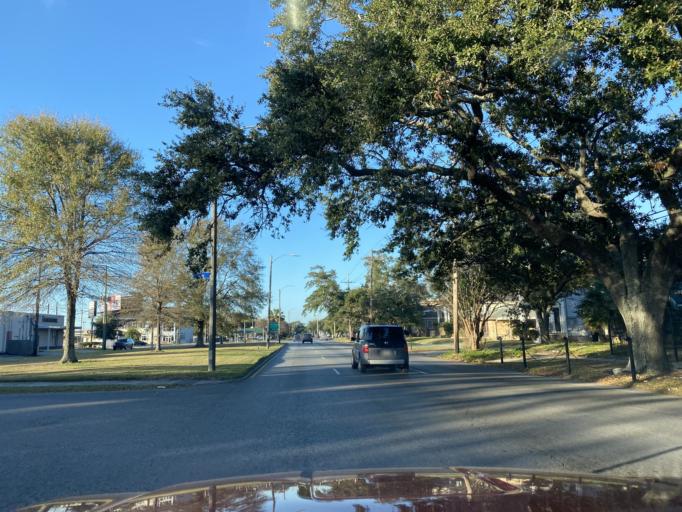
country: US
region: Louisiana
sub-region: Orleans Parish
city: New Orleans
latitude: 29.9979
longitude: -90.0590
